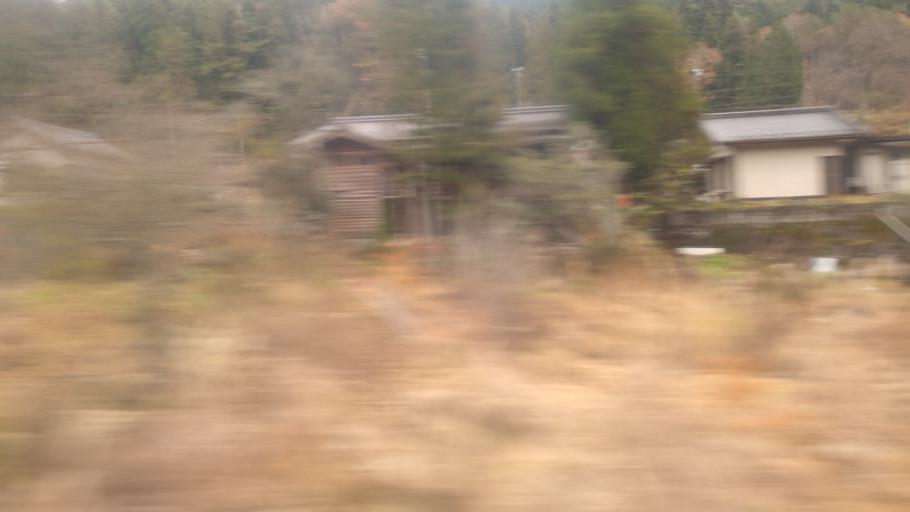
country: JP
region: Gifu
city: Nakatsugawa
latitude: 35.6664
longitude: 137.6278
